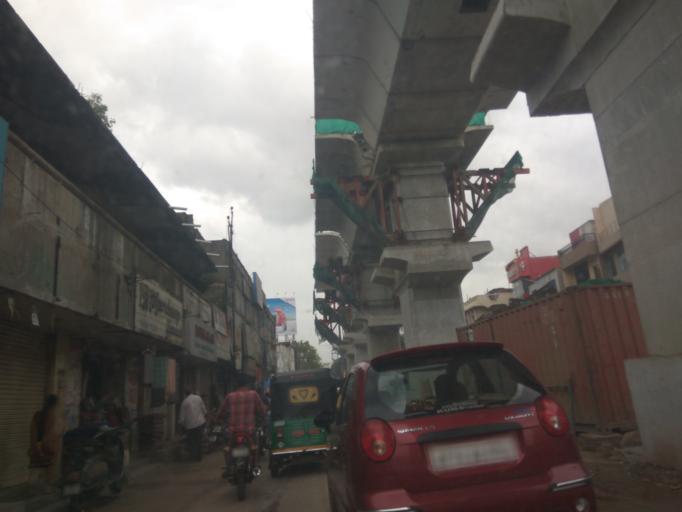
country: IN
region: Telangana
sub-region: Hyderabad
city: Hyderabad
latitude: 17.4007
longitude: 78.4949
